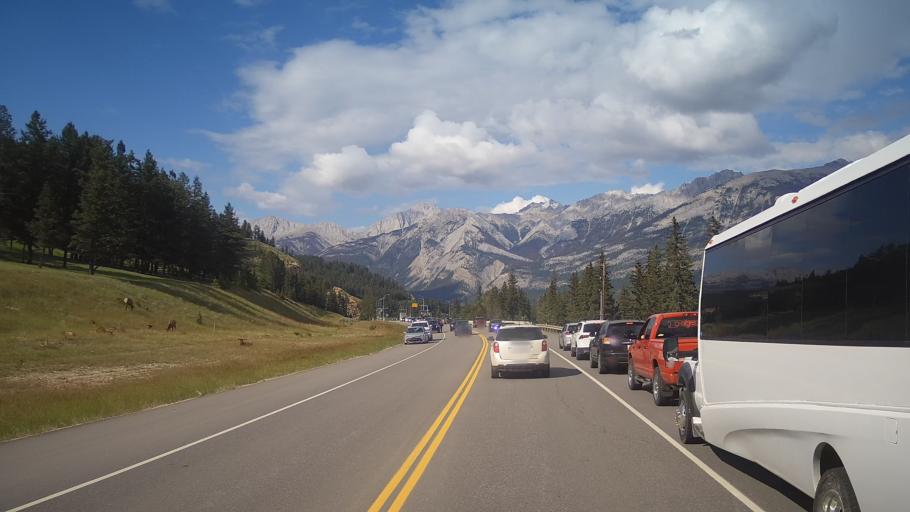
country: CA
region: Alberta
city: Jasper Park Lodge
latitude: 52.9065
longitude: -118.0631
